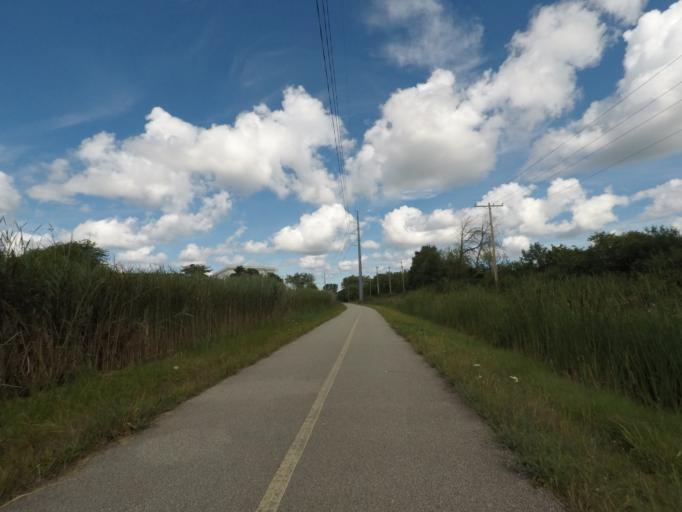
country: US
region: Wisconsin
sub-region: Waukesha County
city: Pewaukee
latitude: 43.0484
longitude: -88.2734
